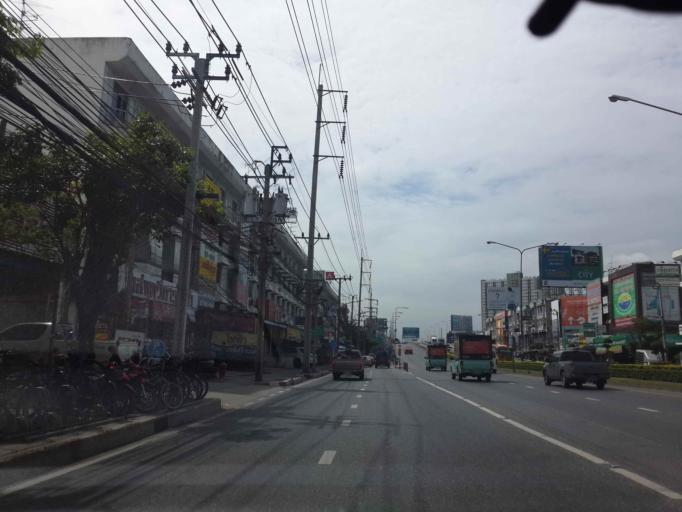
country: TH
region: Bangkok
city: Khan Na Yao
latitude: 13.8406
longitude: 100.6590
